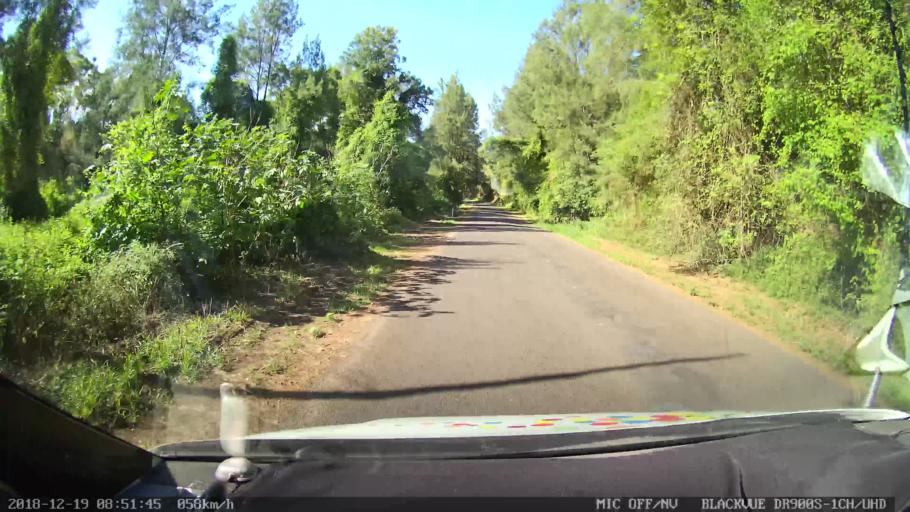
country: AU
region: New South Wales
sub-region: Kyogle
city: Kyogle
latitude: -28.3903
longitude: 152.9786
